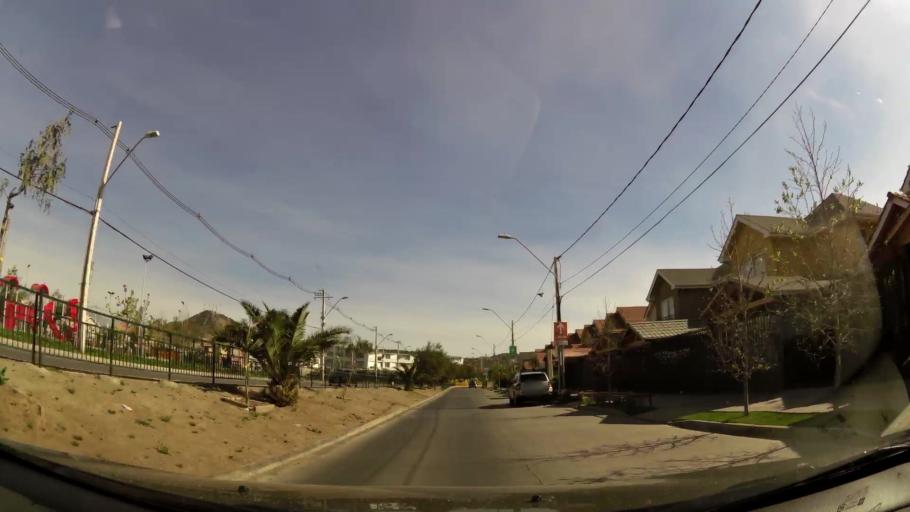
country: CL
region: Santiago Metropolitan
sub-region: Provincia de Cordillera
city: Puente Alto
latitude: -33.5942
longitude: -70.5451
